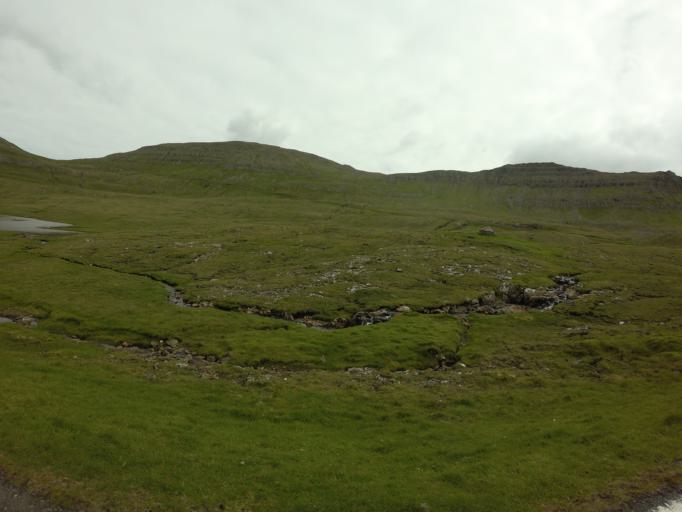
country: FO
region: Suduroy
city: Tvoroyri
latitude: 61.5170
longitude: -6.8482
